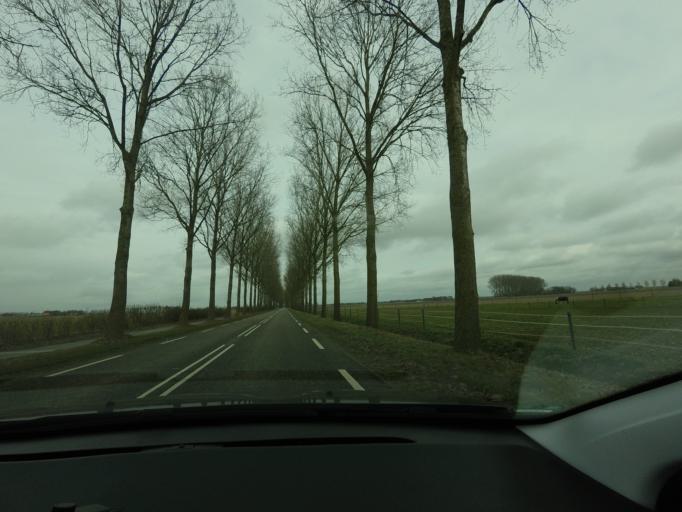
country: NL
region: Friesland
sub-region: Gemeente Lemsterland
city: Lemmer
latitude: 52.7815
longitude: 5.6772
